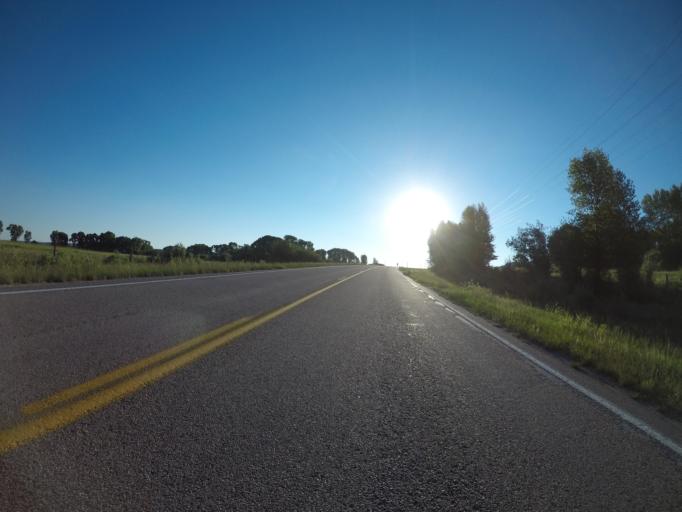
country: US
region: Wyoming
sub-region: Sublette County
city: Marbleton
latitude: 42.5754
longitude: -109.9355
